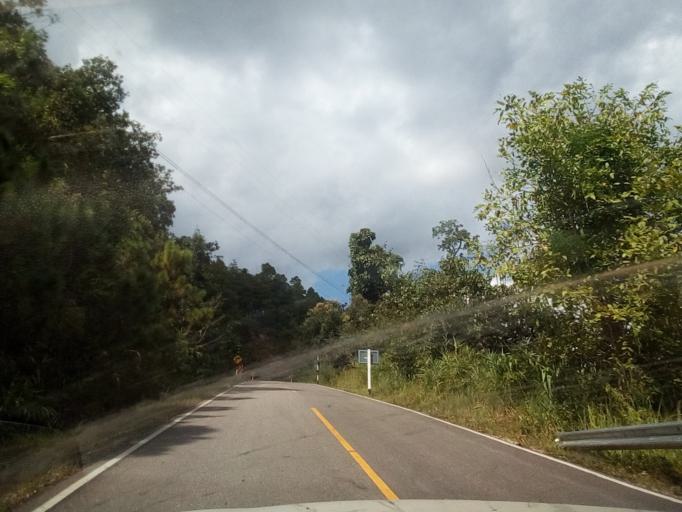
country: TH
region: Chiang Mai
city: Samoeng
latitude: 18.9049
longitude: 98.6757
